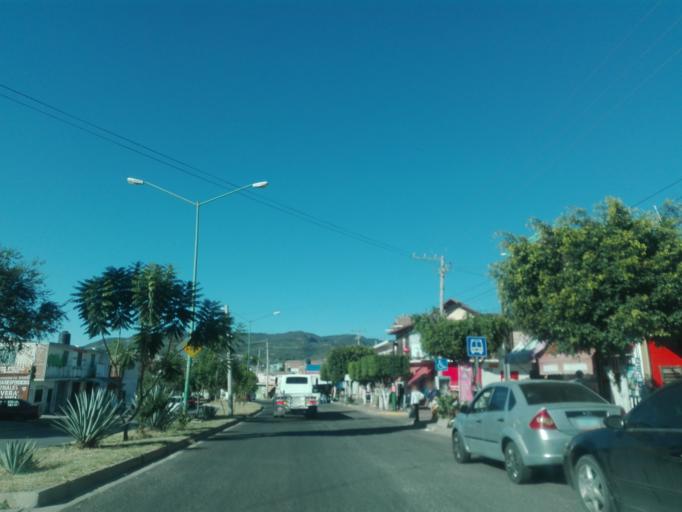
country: MX
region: Guanajuato
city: Leon
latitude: 21.1799
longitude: -101.6747
